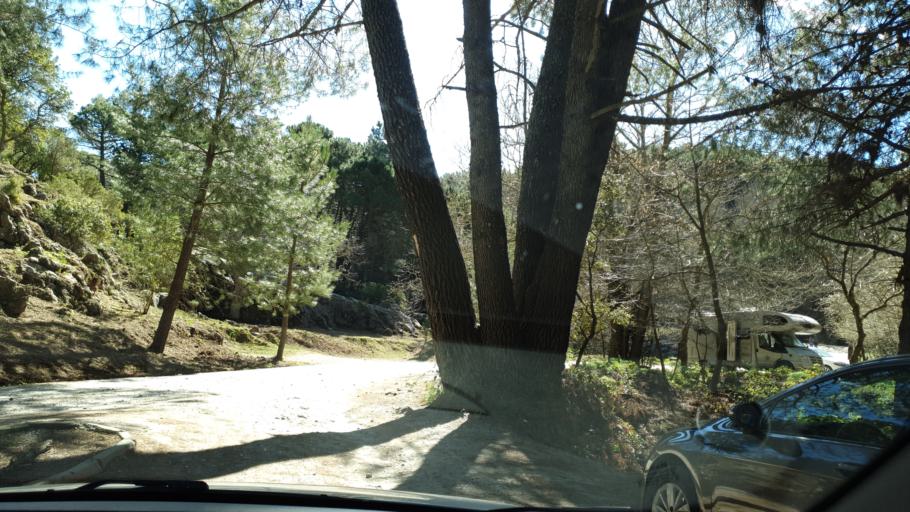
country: ES
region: Andalusia
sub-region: Provincia de Malaga
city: Ojen
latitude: 36.5787
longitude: -4.8844
